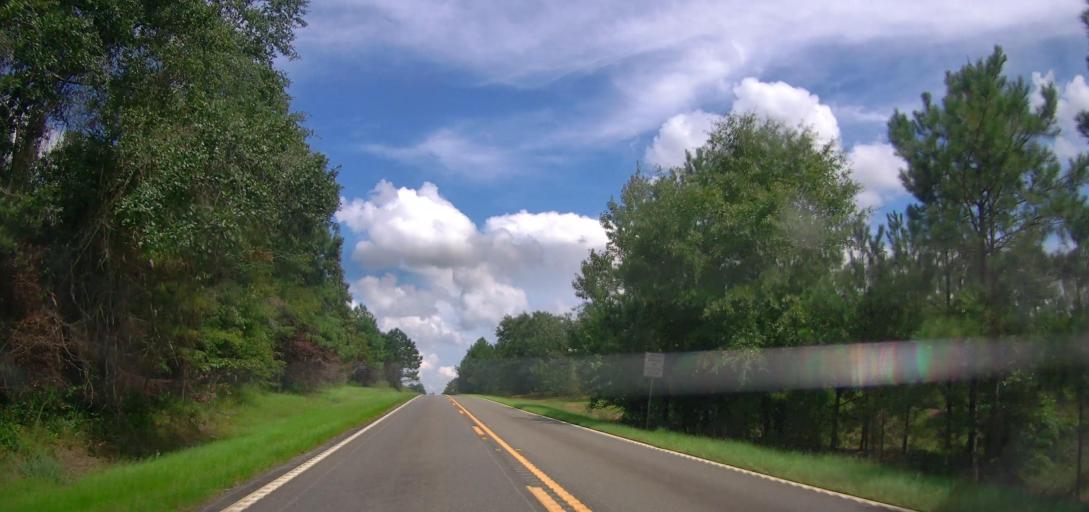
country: US
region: Georgia
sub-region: Taylor County
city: Butler
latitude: 32.4345
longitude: -84.1743
